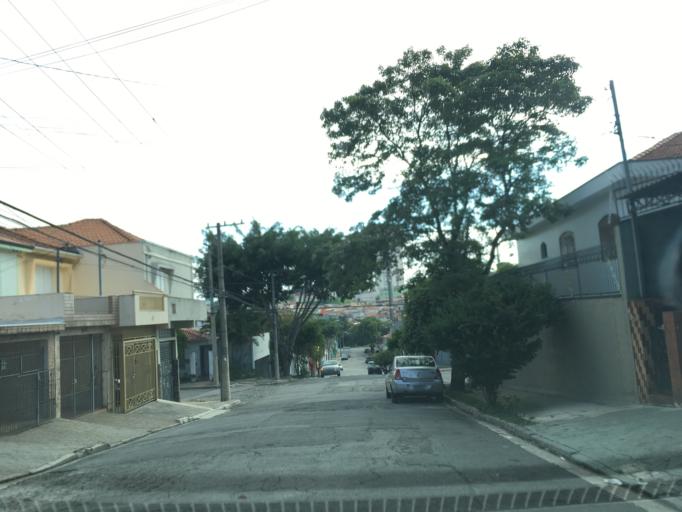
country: BR
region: Sao Paulo
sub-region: Sao Caetano Do Sul
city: Sao Caetano do Sul
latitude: -23.5663
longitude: -46.5718
